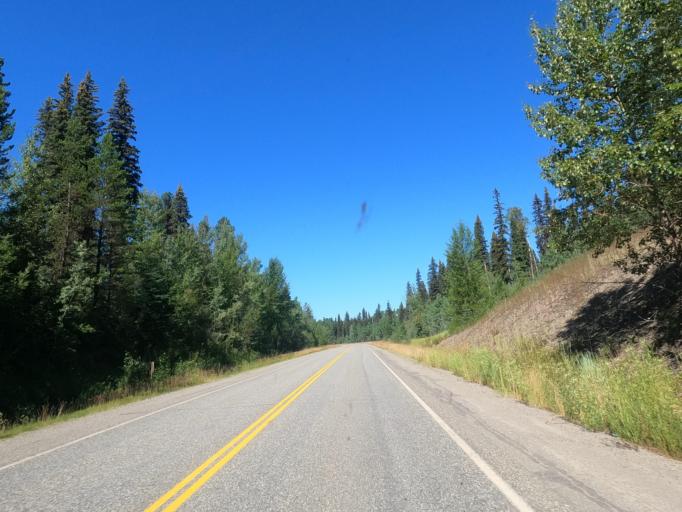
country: CA
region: British Columbia
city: Quesnel
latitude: 53.0545
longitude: -122.1648
